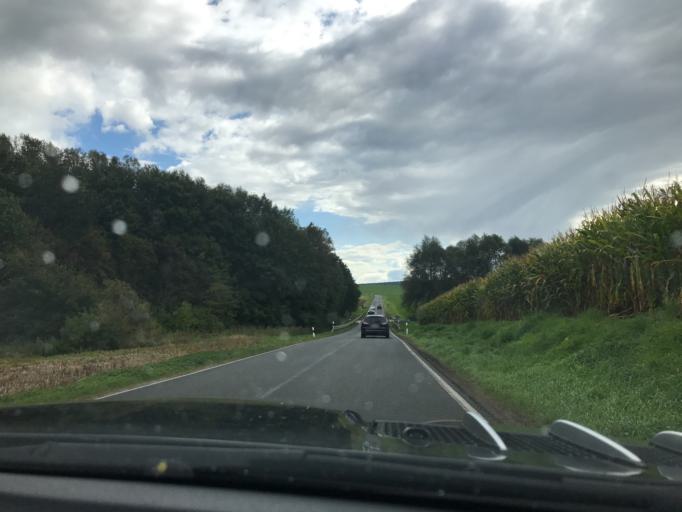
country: DE
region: Thuringia
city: Flarchheim
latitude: 51.1415
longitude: 10.4668
